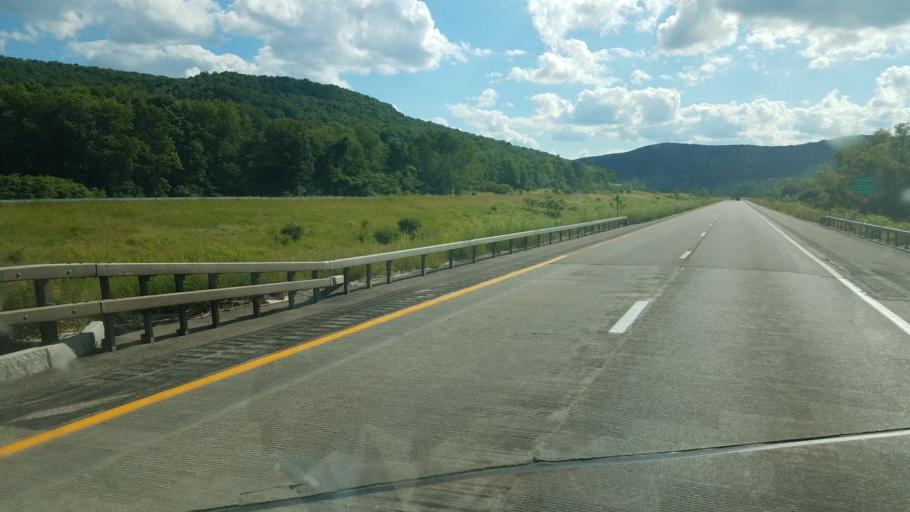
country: US
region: New York
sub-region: Allegany County
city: Cuba
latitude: 42.2163
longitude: -78.3084
